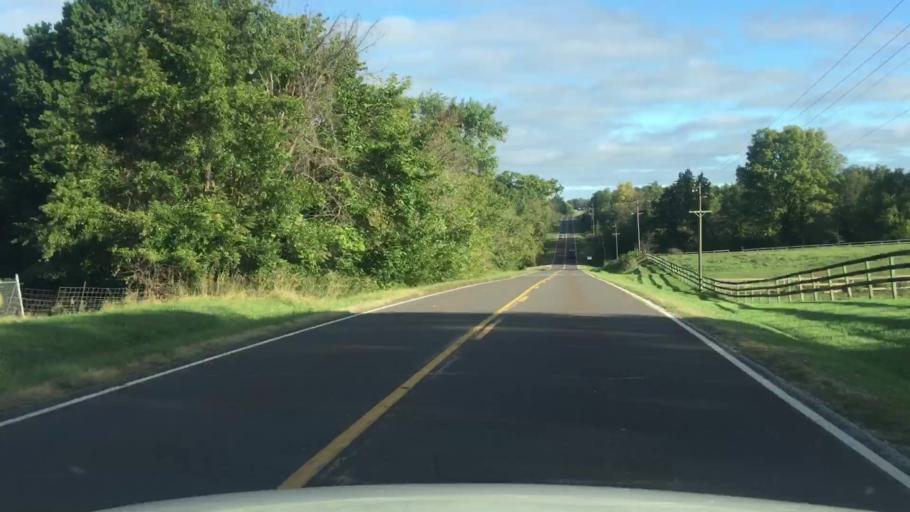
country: US
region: Missouri
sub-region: Howard County
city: New Franklin
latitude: 39.0466
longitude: -92.7444
